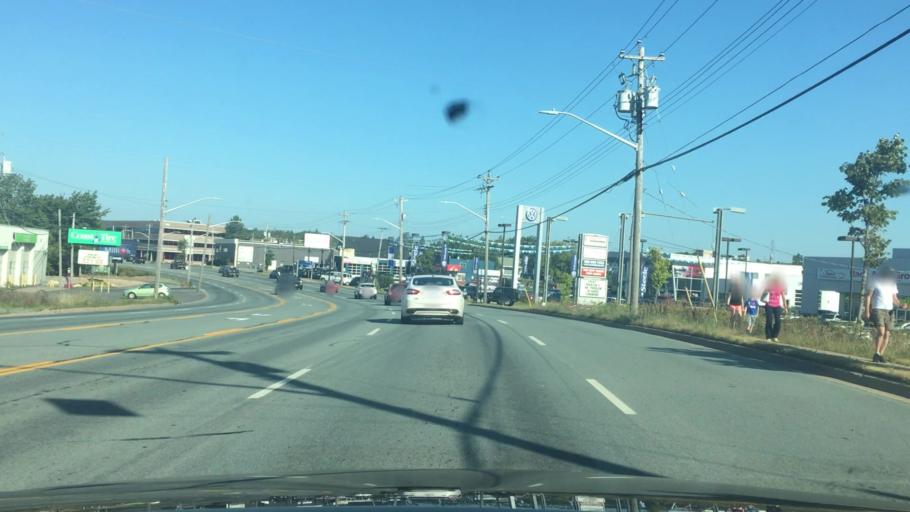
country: CA
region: Nova Scotia
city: Dartmouth
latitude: 44.7012
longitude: -63.6072
